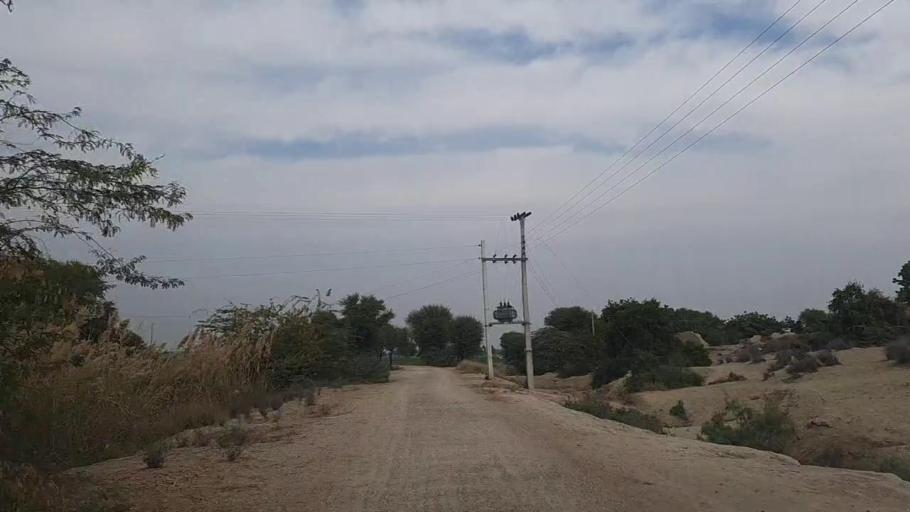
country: PK
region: Sindh
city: Daur
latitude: 26.4375
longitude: 68.4706
